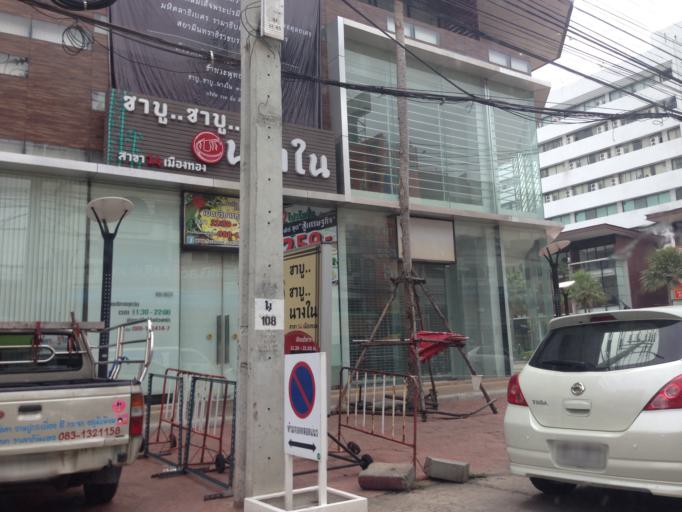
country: TH
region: Nonthaburi
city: Pak Kret
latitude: 13.9135
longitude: 100.5396
